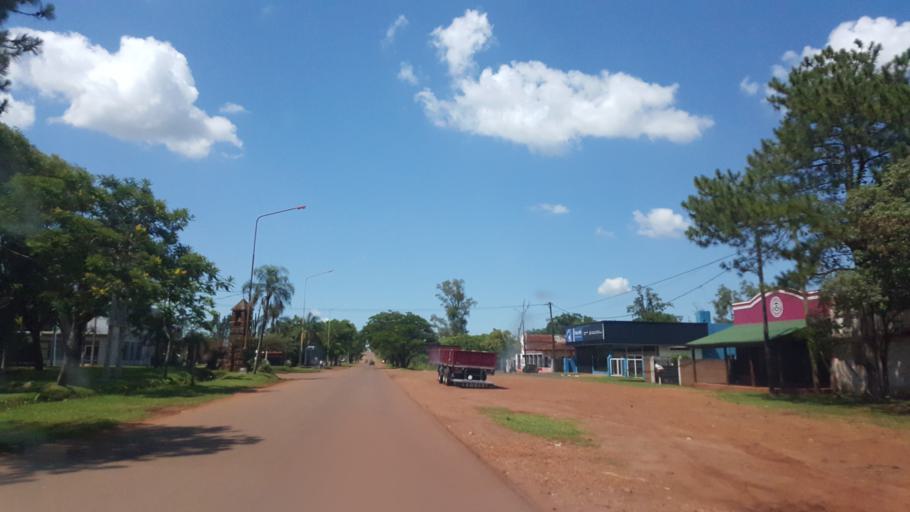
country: AR
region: Corrientes
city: Santo Tome
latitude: -28.5443
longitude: -56.0492
